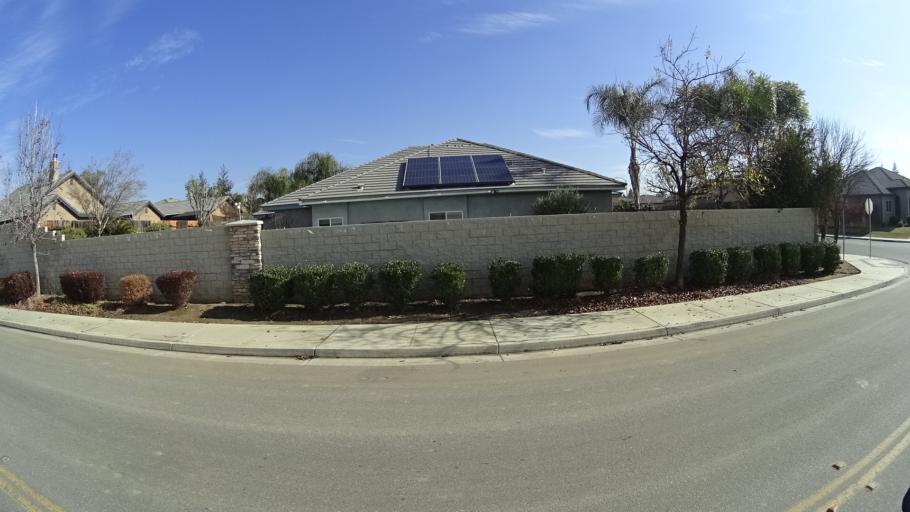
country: US
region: California
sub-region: Kern County
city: Lamont
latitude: 35.3887
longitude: -118.8848
